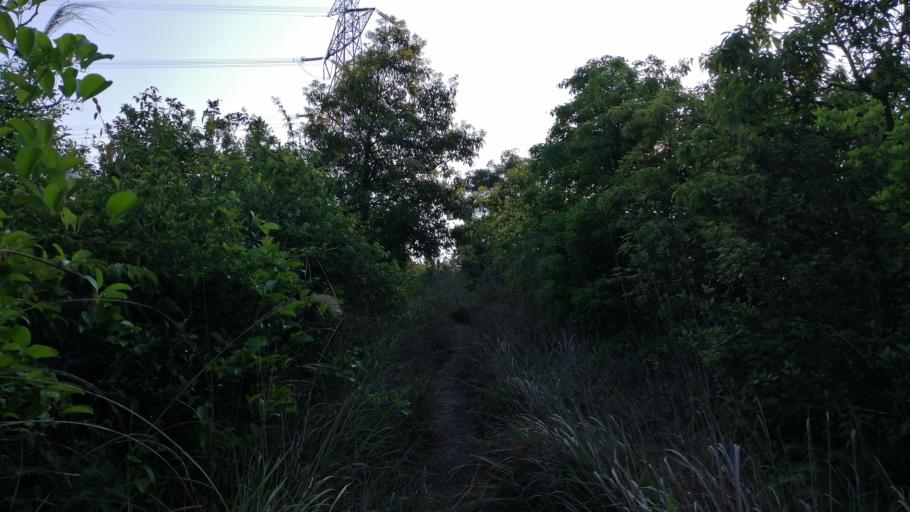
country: HK
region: Tai Po
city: Tai Po
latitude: 22.4382
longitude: 114.1507
